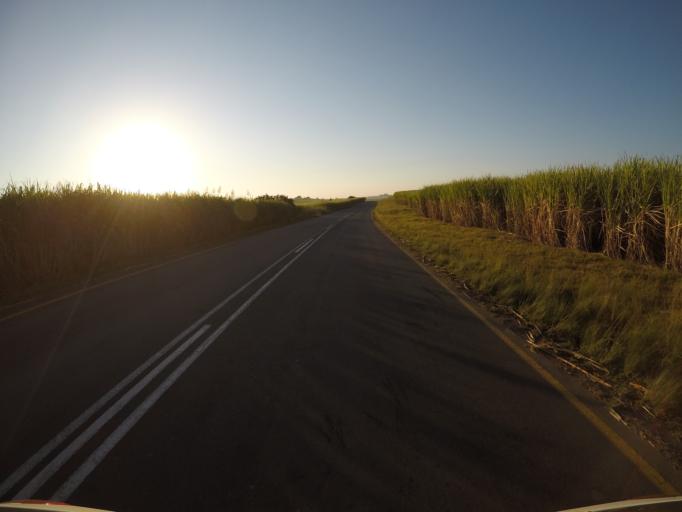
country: ZA
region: KwaZulu-Natal
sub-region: uThungulu District Municipality
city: eSikhawini
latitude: -28.9490
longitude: 31.7002
